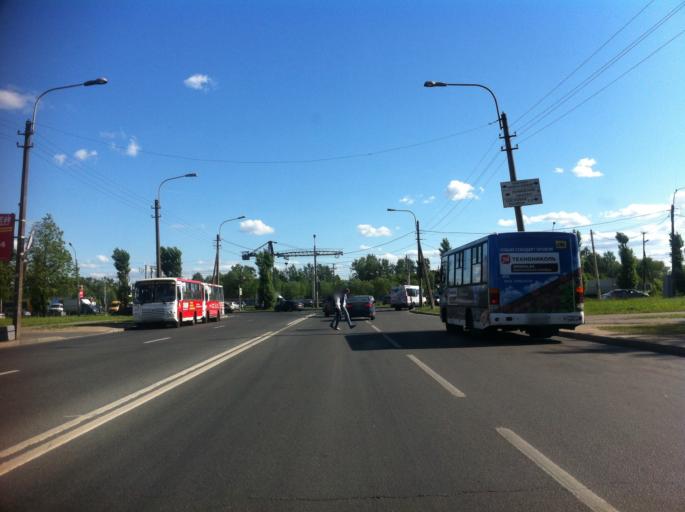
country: RU
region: St.-Petersburg
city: Uritsk
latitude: 59.8248
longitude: 30.1758
